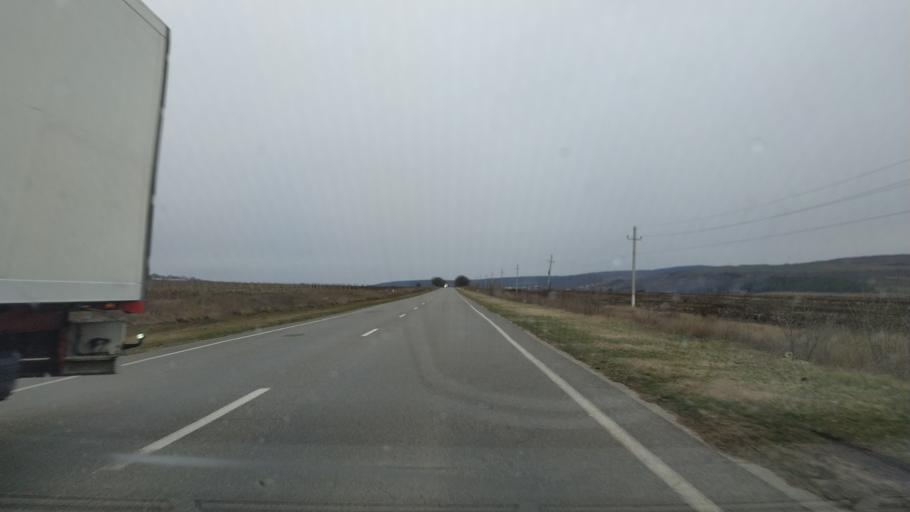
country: MD
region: Hincesti
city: Hincesti
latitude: 46.7658
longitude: 28.5232
